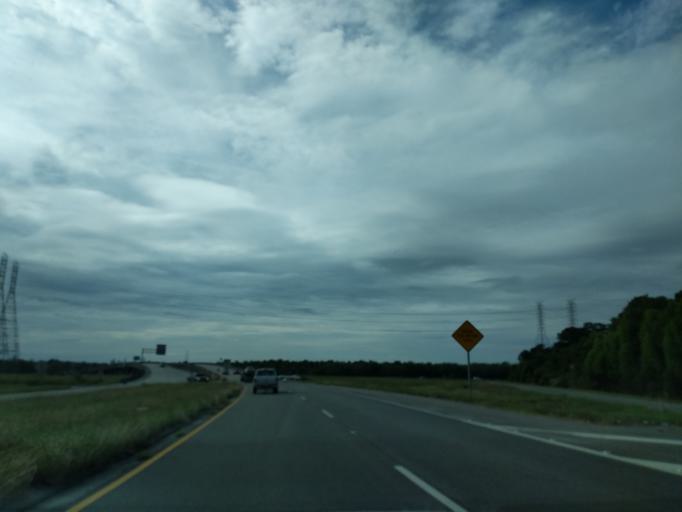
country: US
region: Louisiana
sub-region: Saint Bernard Parish
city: Chalmette
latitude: 30.0175
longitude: -89.9358
